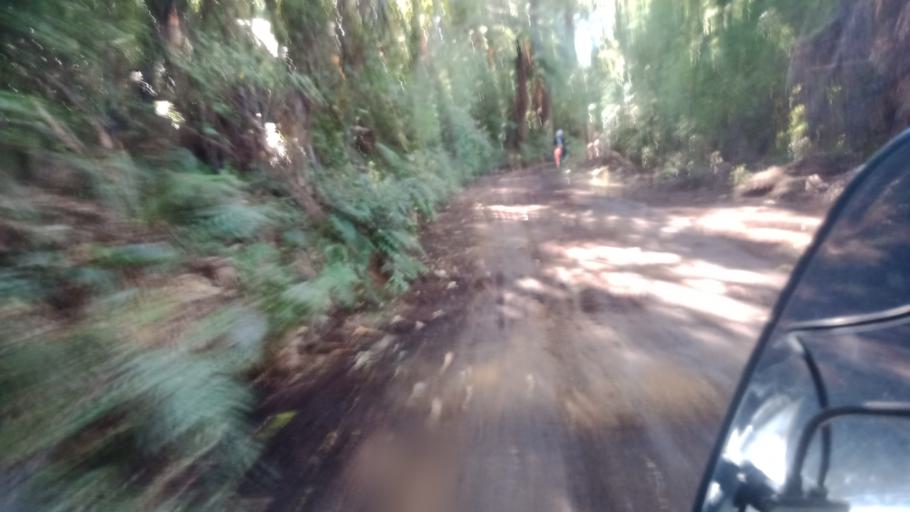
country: NZ
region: Hawke's Bay
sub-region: Wairoa District
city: Wairoa
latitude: -39.0056
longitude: 177.0560
